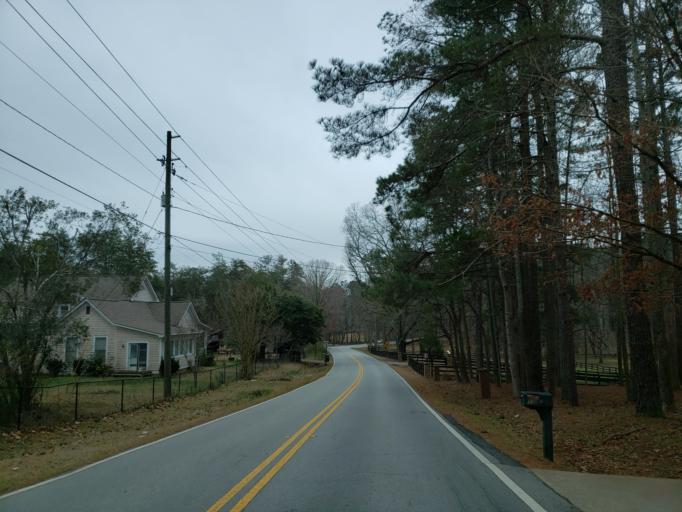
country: US
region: Georgia
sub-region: Paulding County
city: Hiram
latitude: 33.9282
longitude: -84.7188
